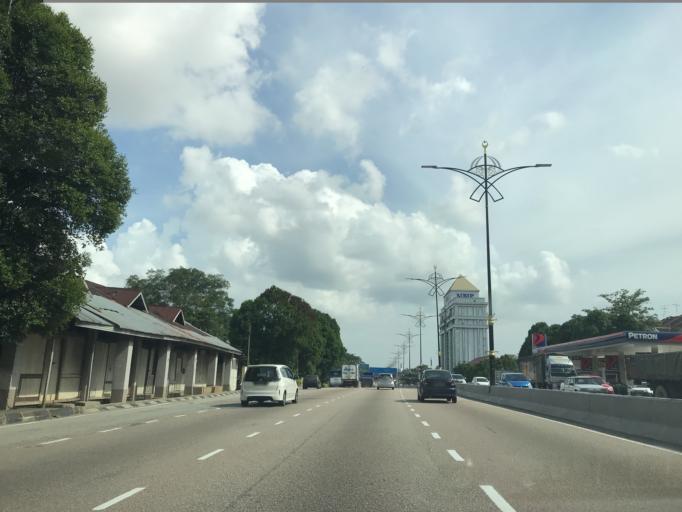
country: MY
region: Johor
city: Skudai
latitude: 1.5401
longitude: 103.6604
